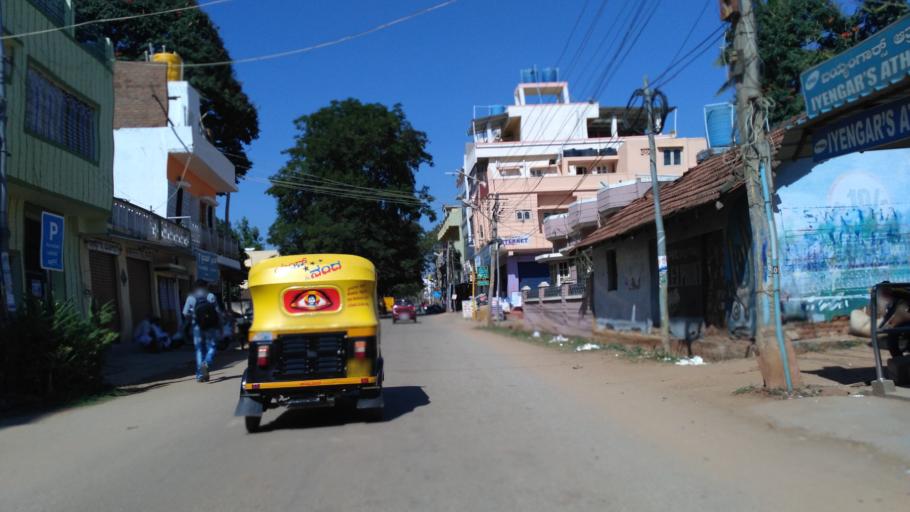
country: IN
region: Karnataka
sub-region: Hassan
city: Hassan
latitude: 13.0084
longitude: 76.1062
